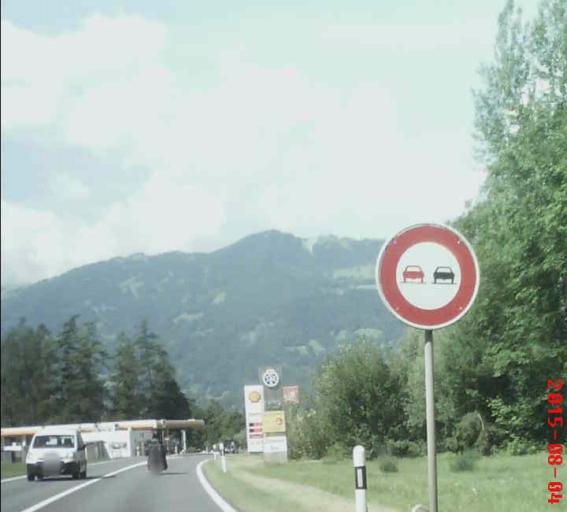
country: CH
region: Grisons
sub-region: Landquart District
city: Malans
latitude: 46.9717
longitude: 9.6007
